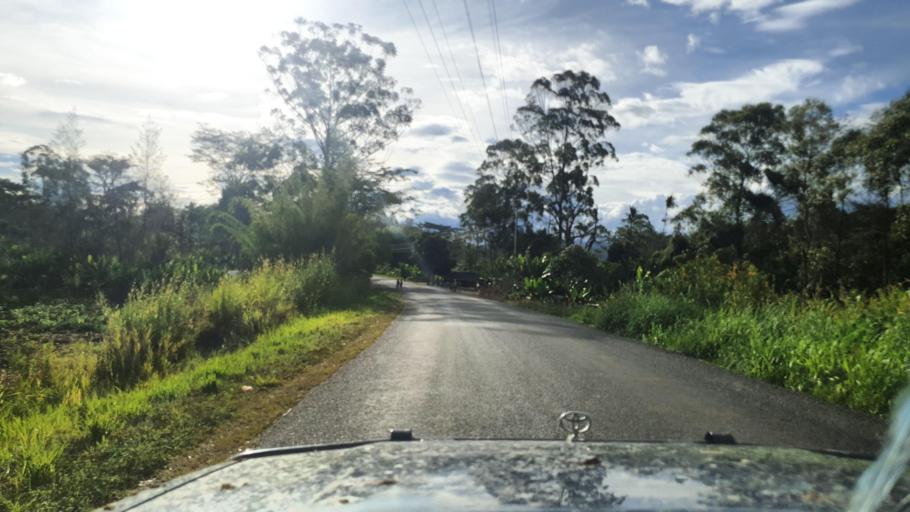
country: PG
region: Jiwaka
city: Minj
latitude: -5.8763
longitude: 144.7161
